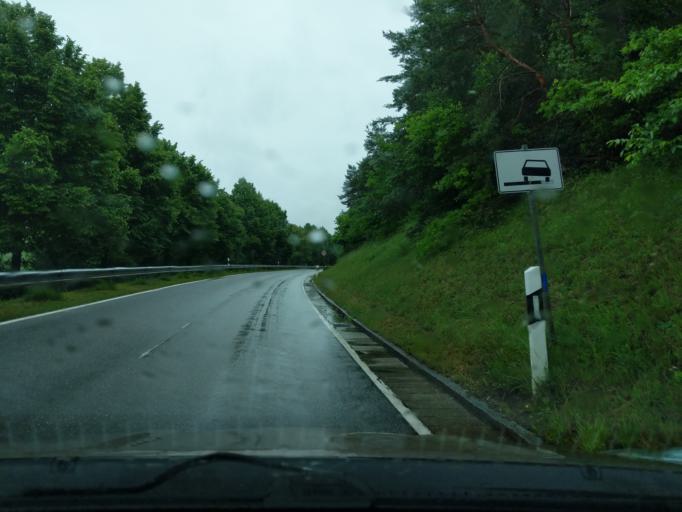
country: DE
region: Bavaria
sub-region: Upper Palatinate
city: Pettendorf
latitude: 49.0372
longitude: 12.0279
